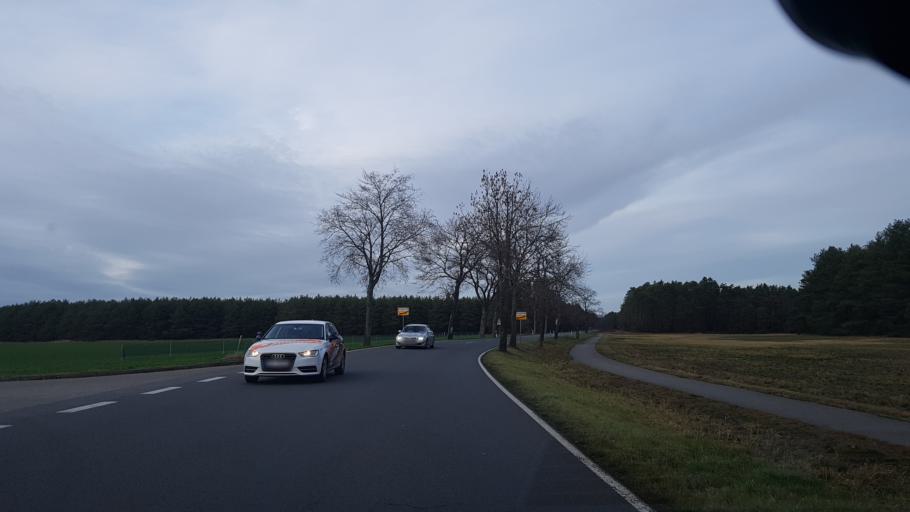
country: DE
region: Brandenburg
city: Schilda
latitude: 51.5790
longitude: 13.3575
